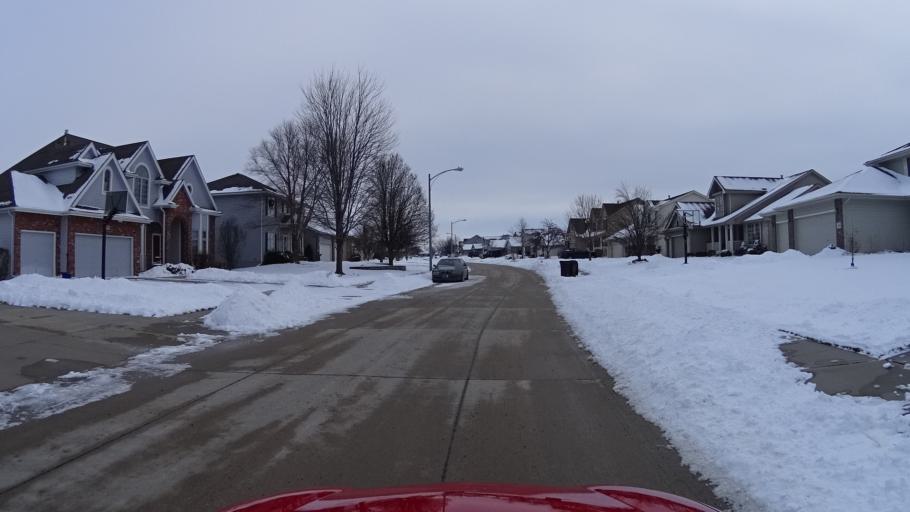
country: US
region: Nebraska
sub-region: Sarpy County
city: Offutt Air Force Base
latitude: 41.1101
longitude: -95.9433
